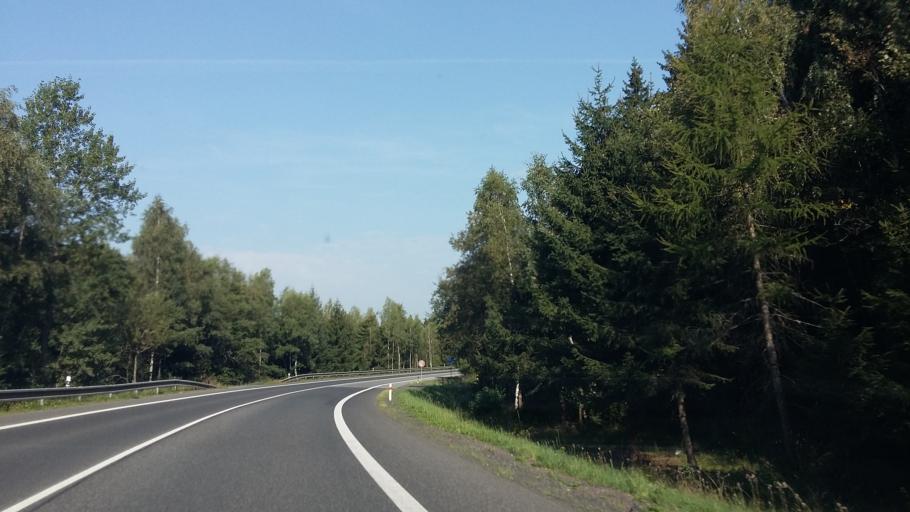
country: CZ
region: Liberecky
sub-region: Okres Jablonec nad Nisou
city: Jablonec nad Nisou
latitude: 50.7050
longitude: 15.1427
